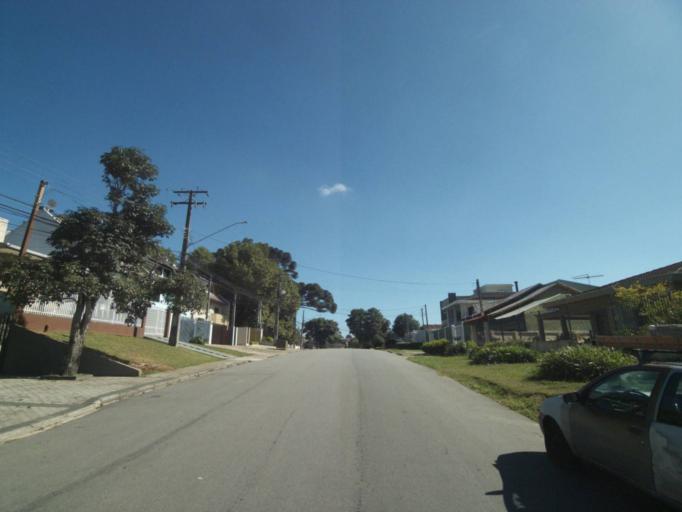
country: BR
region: Parana
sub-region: Pinhais
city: Pinhais
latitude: -25.4376
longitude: -49.2290
